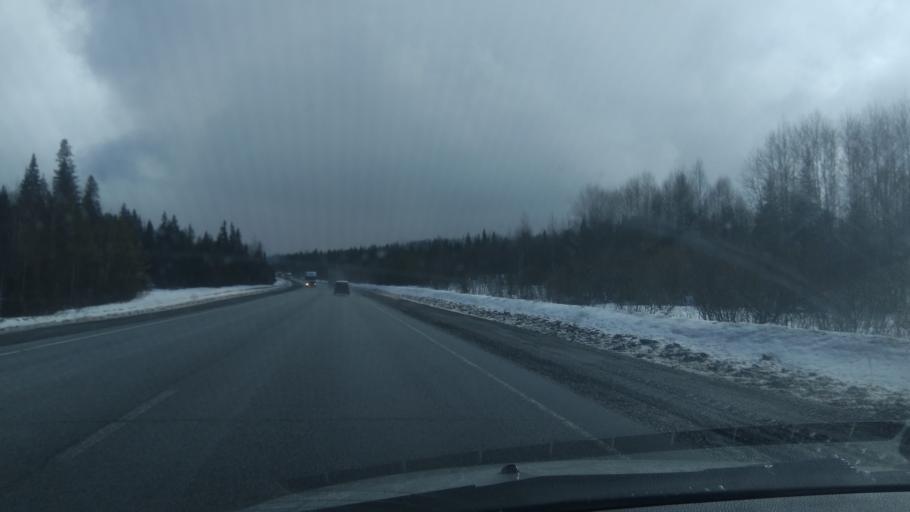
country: RU
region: Sverdlovsk
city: Arti
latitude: 56.7903
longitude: 58.5004
